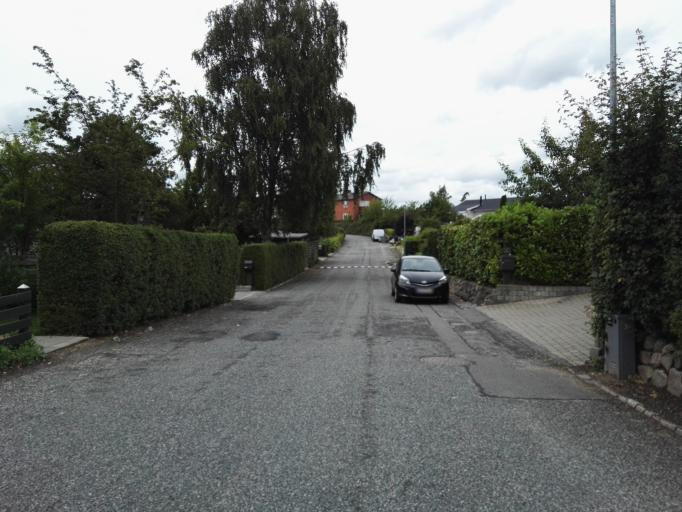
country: DK
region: Capital Region
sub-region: Egedal Kommune
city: Stenlose
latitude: 55.7705
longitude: 12.2040
